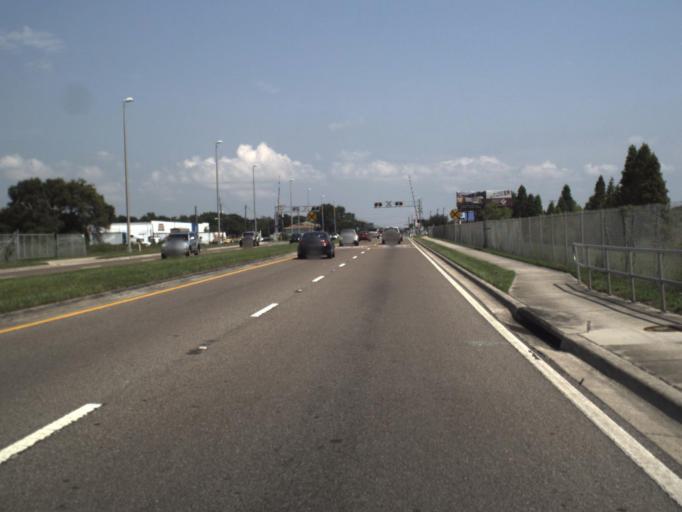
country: US
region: Florida
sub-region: Hillsborough County
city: Tampa
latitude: 27.8974
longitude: -82.5062
